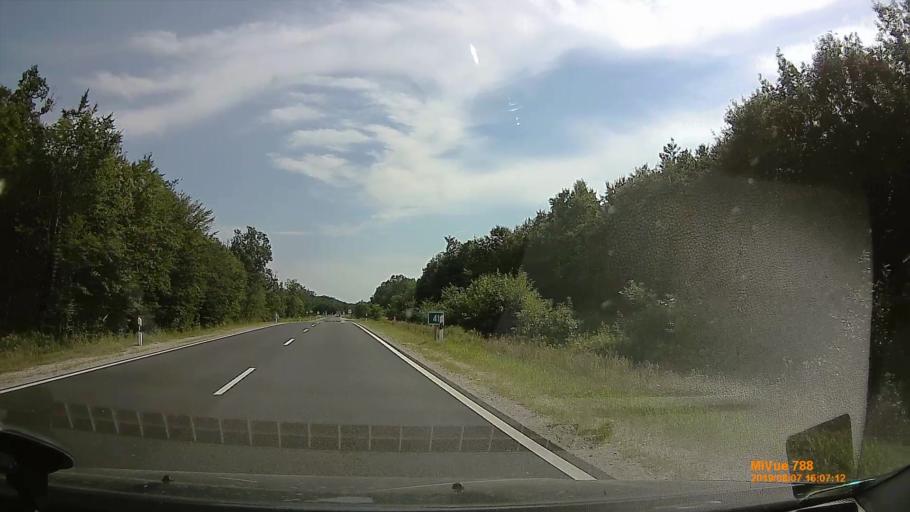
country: HU
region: Zala
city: Zalalovo
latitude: 46.9246
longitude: 16.6000
